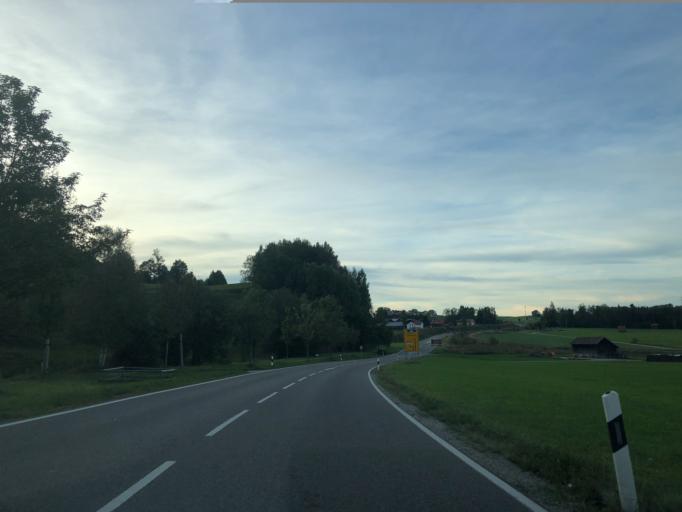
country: DE
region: Bavaria
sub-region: Swabia
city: Pfronten
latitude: 47.6010
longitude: 10.5431
